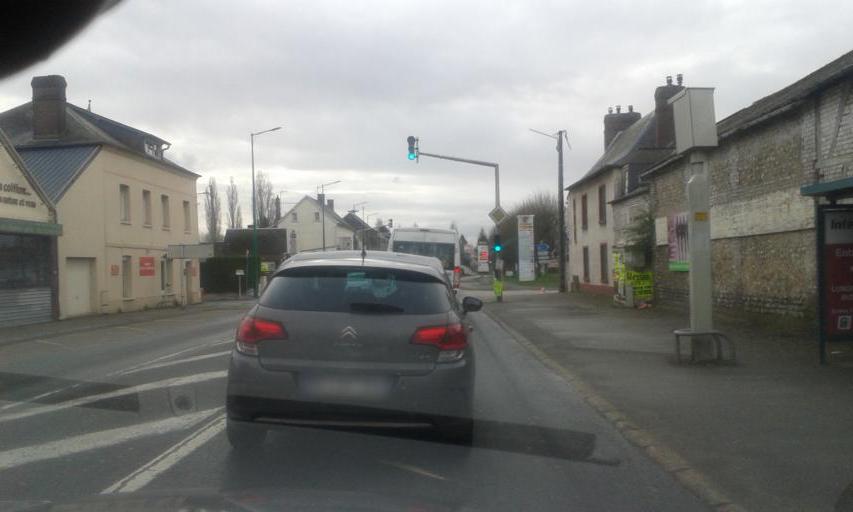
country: FR
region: Haute-Normandie
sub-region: Departement de la Seine-Maritime
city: Boos
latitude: 49.3898
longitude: 1.1989
